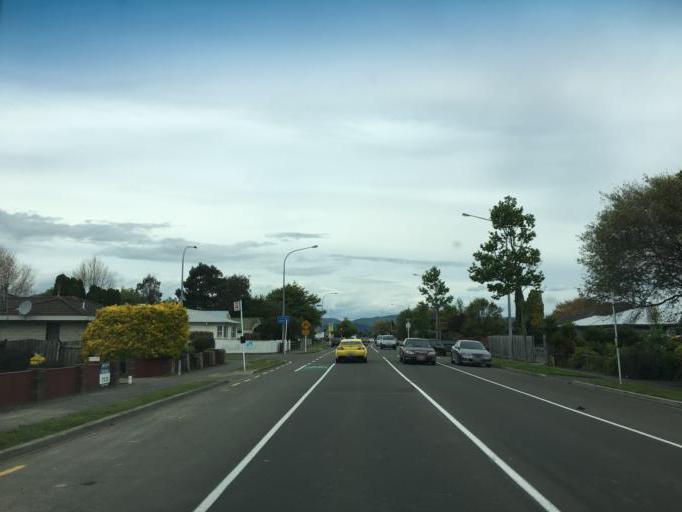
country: NZ
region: Manawatu-Wanganui
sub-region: Palmerston North City
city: Palmerston North
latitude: -40.3622
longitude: 175.5935
